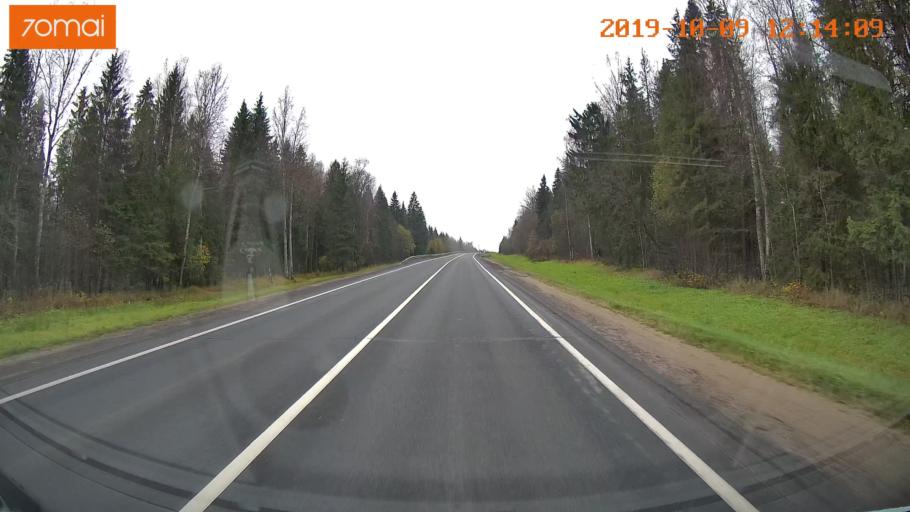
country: RU
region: Jaroslavl
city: Prechistoye
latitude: 58.5000
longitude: 40.3404
